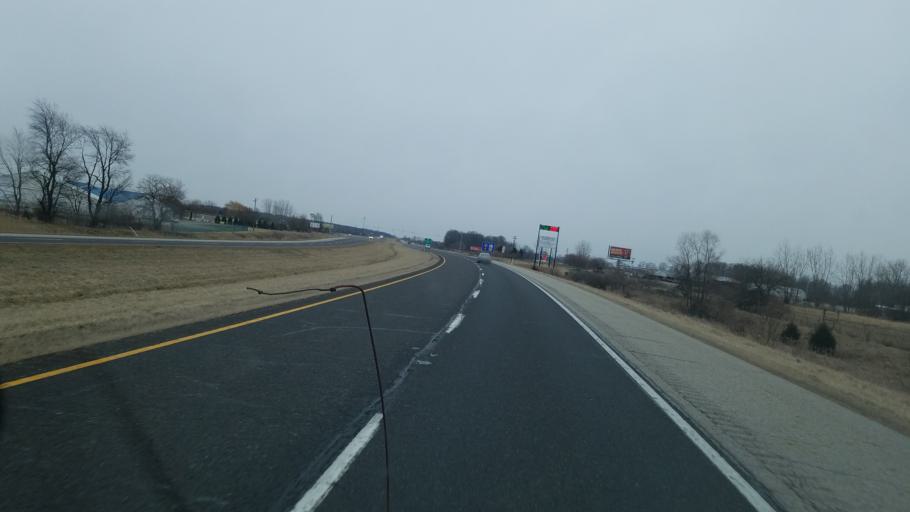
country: US
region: Indiana
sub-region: Fulton County
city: Rochester
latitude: 41.0494
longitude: -86.2343
